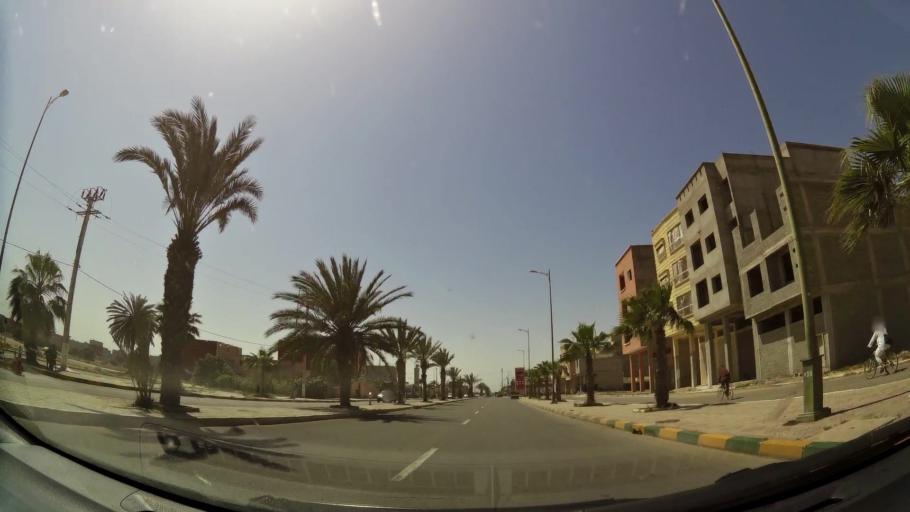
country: MA
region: Souss-Massa-Draa
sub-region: Inezgane-Ait Mellou
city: Inezgane
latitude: 30.3166
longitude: -9.5029
